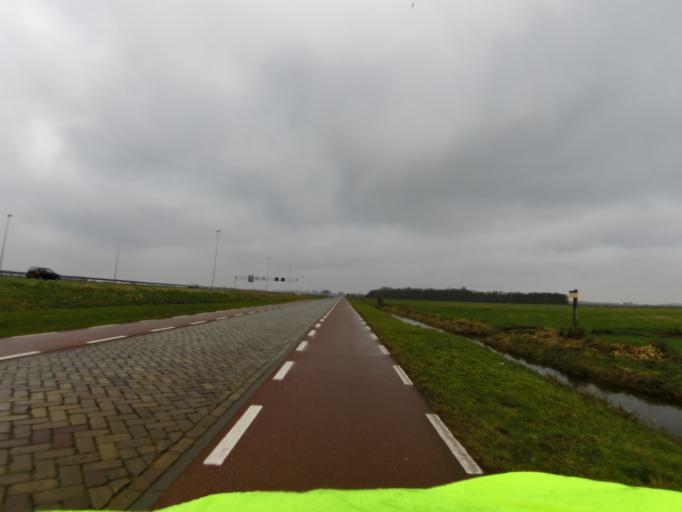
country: NL
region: South Holland
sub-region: Gemeente Vlaardingen
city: Vlaardingen
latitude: 51.9203
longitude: 4.3050
